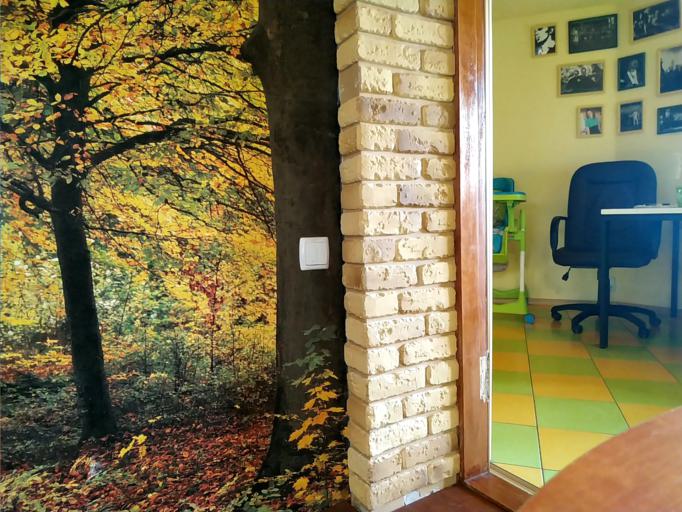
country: RU
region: Jaroslavl
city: Krasnyy Profintern
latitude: 58.0185
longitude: 40.4728
